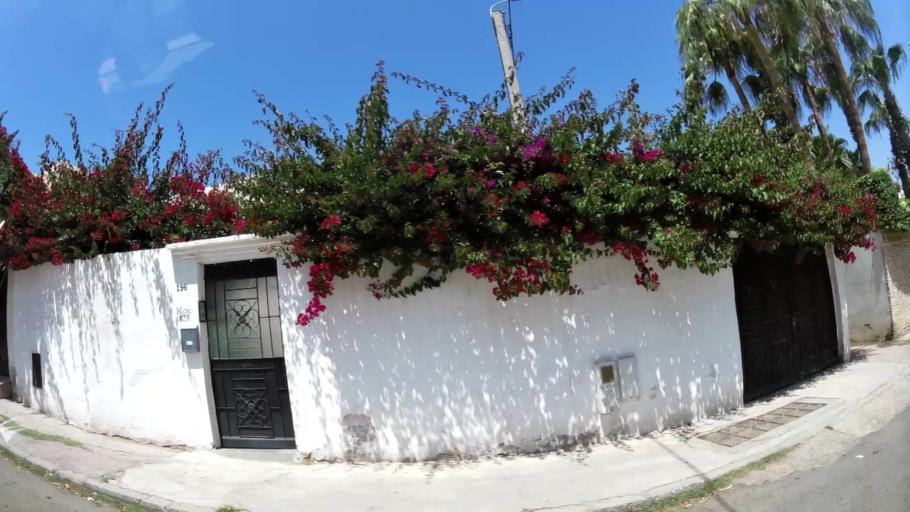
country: MA
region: Souss-Massa-Draa
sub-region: Agadir-Ida-ou-Tnan
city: Agadir
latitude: 30.4339
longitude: -9.5877
